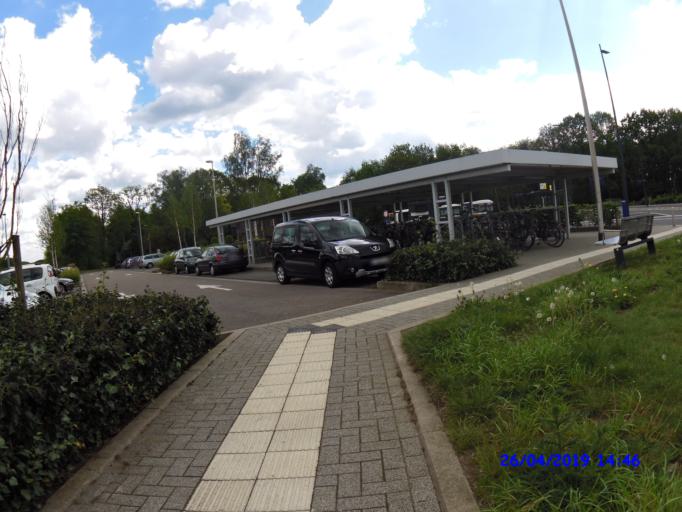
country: BE
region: Flanders
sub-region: Provincie Limburg
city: Beringen
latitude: 51.0506
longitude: 5.2355
